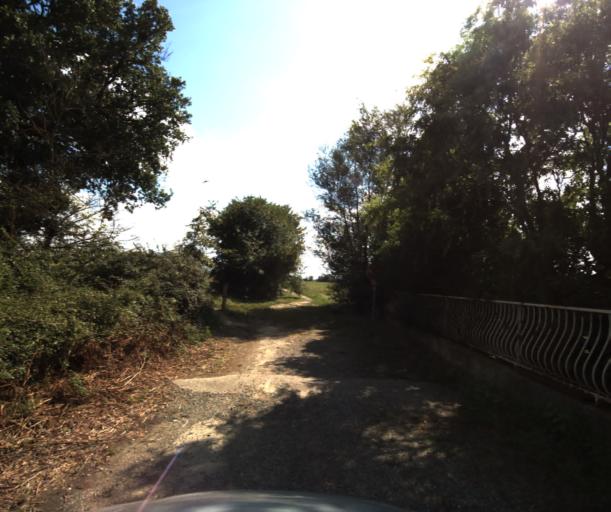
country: FR
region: Midi-Pyrenees
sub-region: Departement de la Haute-Garonne
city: Roquettes
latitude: 43.4923
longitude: 1.3633
